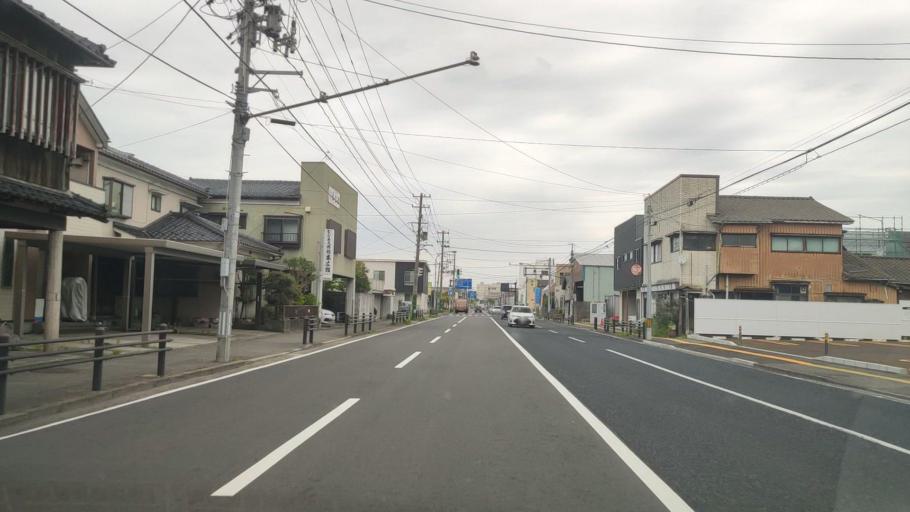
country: JP
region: Niigata
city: Niigata-shi
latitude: 37.9342
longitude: 139.0727
